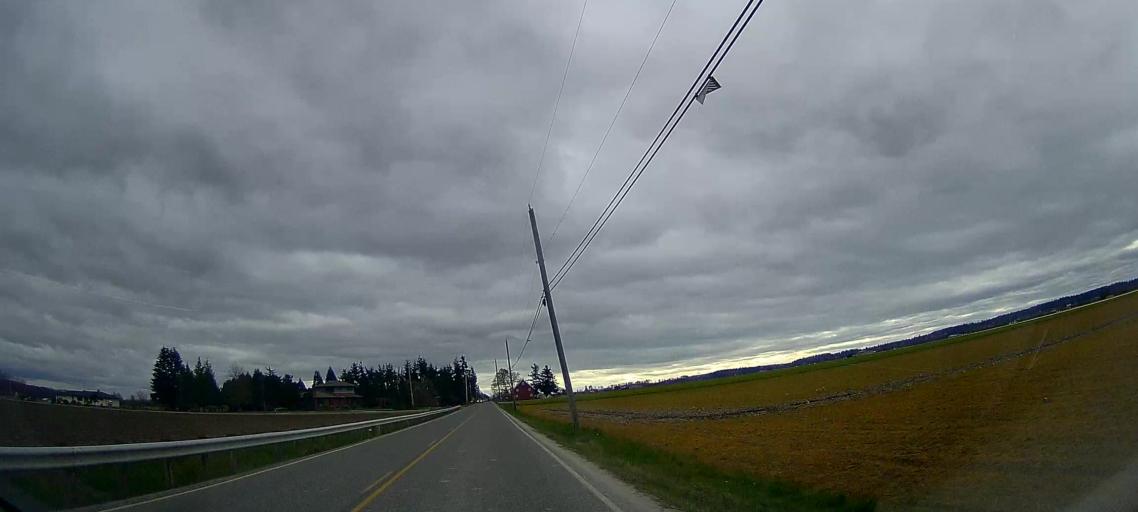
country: US
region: Washington
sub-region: Skagit County
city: Mount Vernon
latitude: 48.4078
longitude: -122.4009
